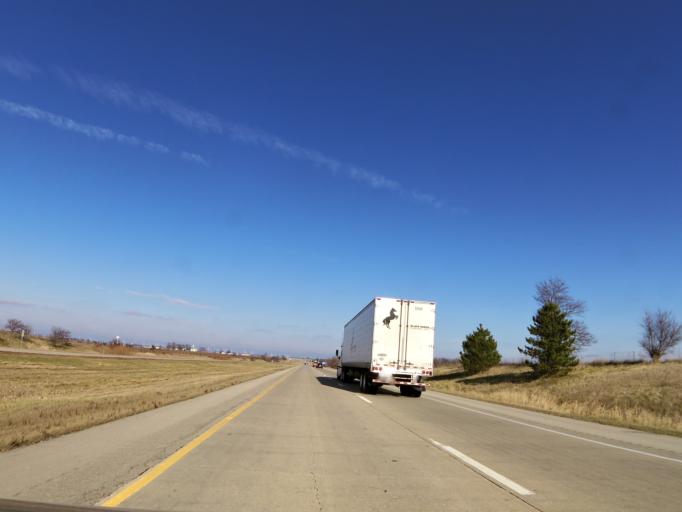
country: US
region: Illinois
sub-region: LaSalle County
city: Mendota
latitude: 41.5271
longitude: -89.0592
